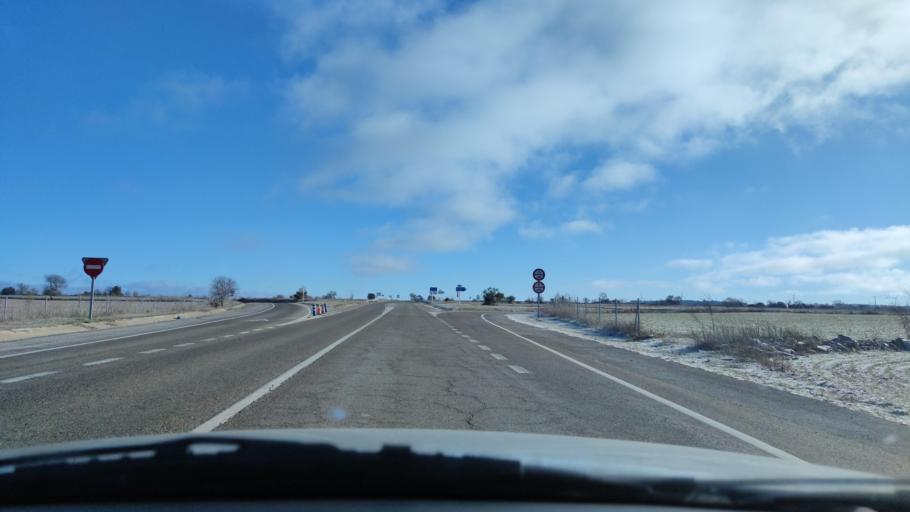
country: ES
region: Catalonia
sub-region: Provincia de Barcelona
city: Pujalt
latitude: 41.7277
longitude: 1.3791
